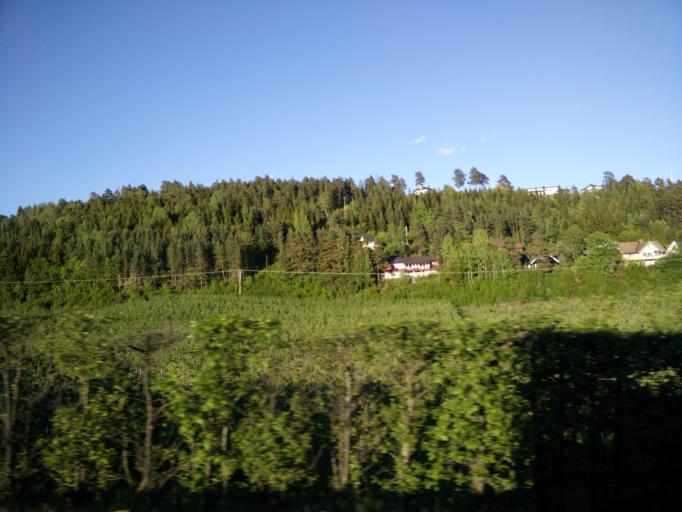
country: NO
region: Buskerud
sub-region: Ringerike
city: Honefoss
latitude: 60.1317
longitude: 10.2742
